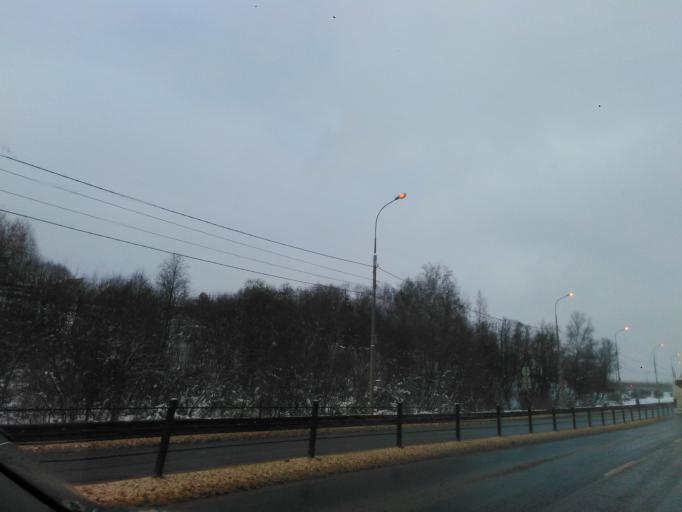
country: RU
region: Moskovskaya
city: Dedenevo
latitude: 56.2558
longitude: 37.5111
